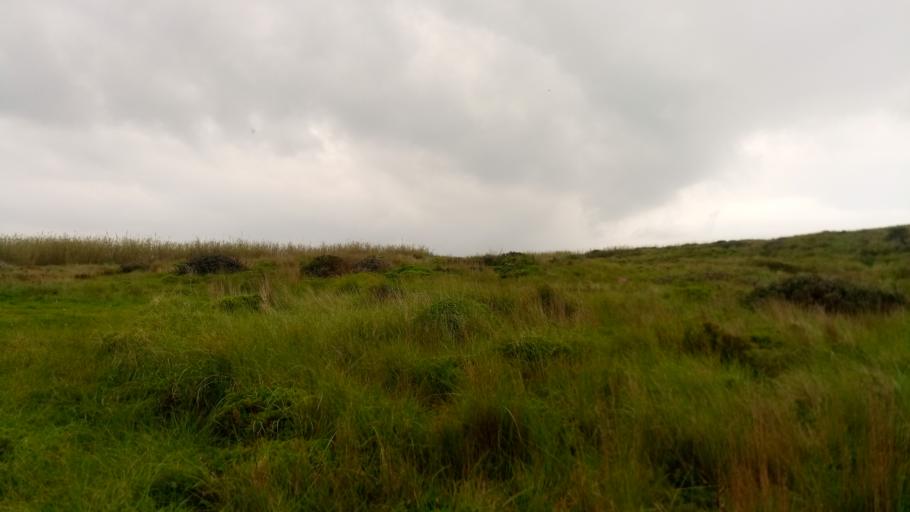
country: PT
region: Leiria
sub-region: Caldas da Rainha
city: Caldas da Rainha
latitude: 39.4678
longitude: -9.2002
